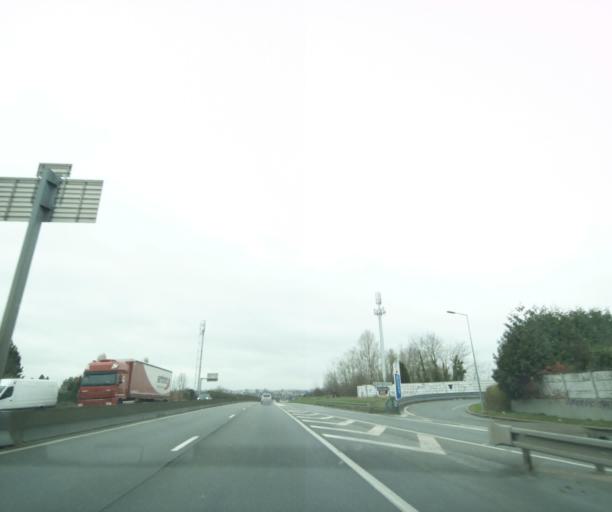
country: FR
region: Ile-de-France
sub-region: Departement de l'Essonne
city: Arpajon
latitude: 48.5970
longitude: 2.2442
